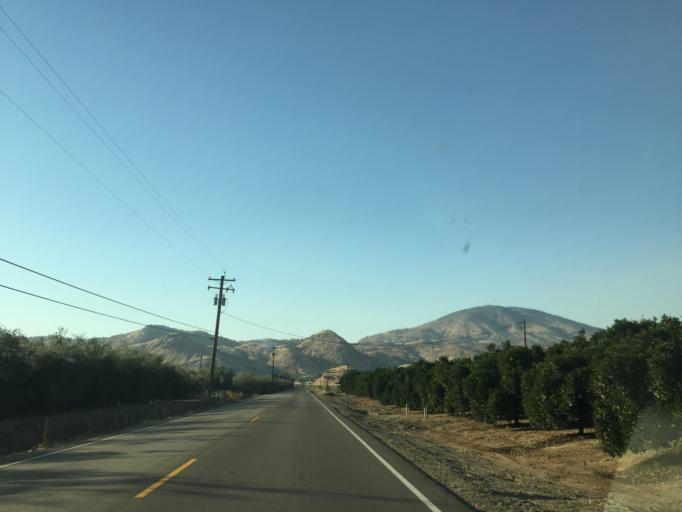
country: US
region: California
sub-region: Fresno County
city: Orange Cove
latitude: 36.6916
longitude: -119.3044
